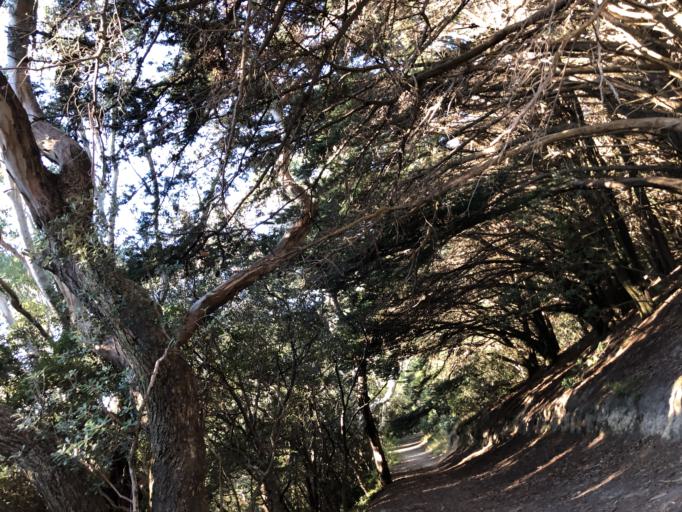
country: NZ
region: Wellington
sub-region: Wellington City
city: Wellington
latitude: -41.2984
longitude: 174.7900
